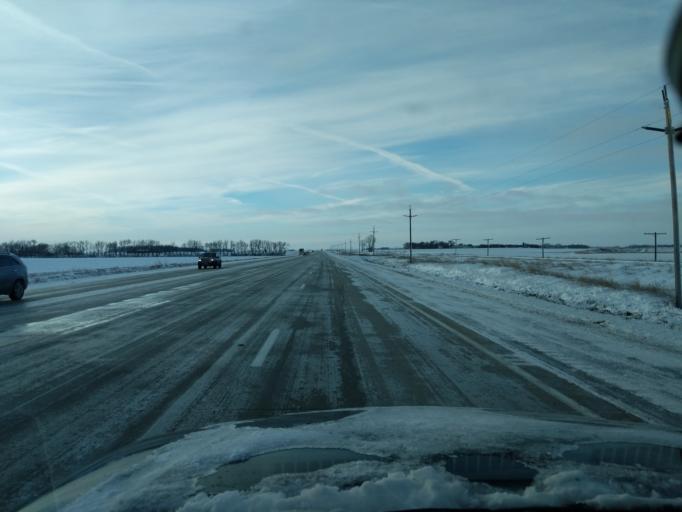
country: US
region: Minnesota
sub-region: Renville County
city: Hector
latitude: 44.7518
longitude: -94.7815
